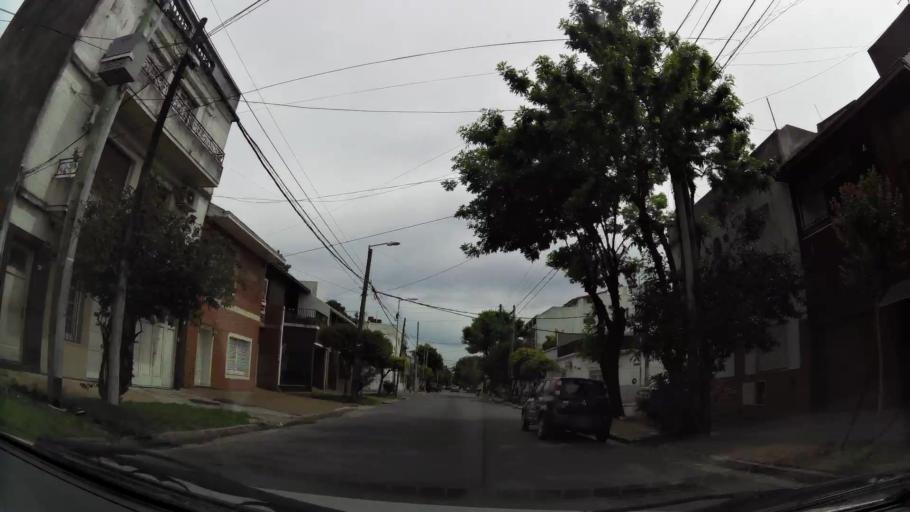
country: AR
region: Buenos Aires
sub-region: Partido de Avellaneda
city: Avellaneda
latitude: -34.6724
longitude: -58.3572
